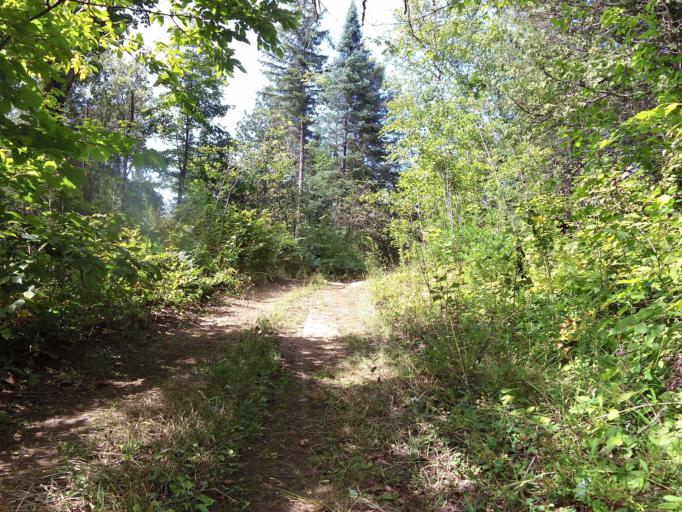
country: CA
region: Ontario
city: Renfrew
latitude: 45.1041
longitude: -76.7096
